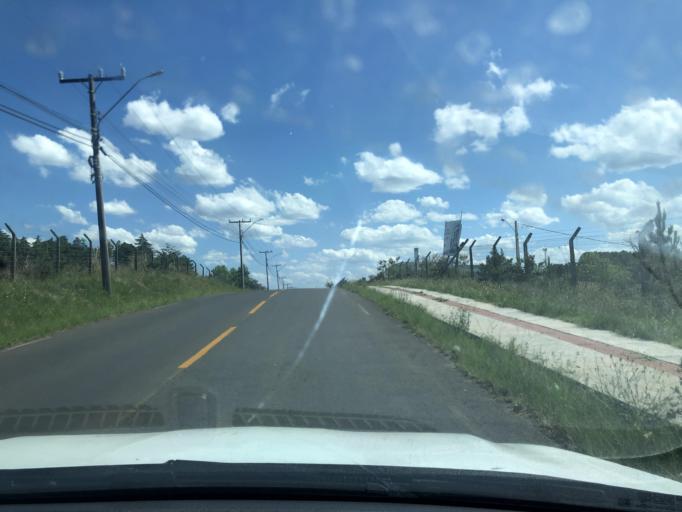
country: BR
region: Santa Catarina
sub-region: Lages
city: Lages
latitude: -27.8022
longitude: -50.3367
